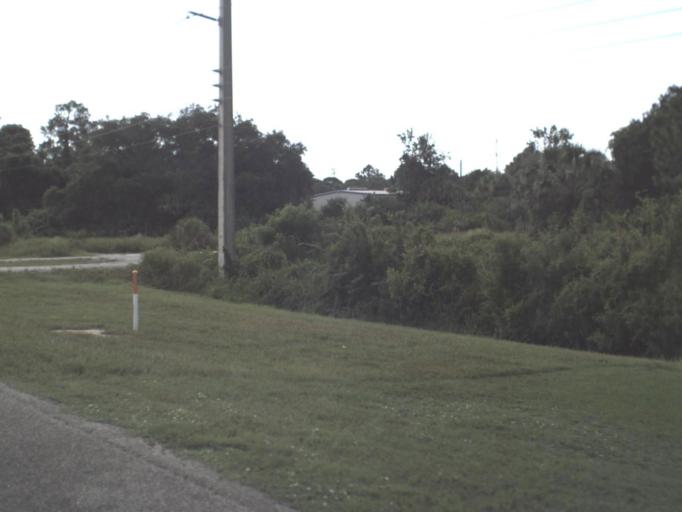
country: US
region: Florida
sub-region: Sarasota County
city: North Port
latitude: 27.0181
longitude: -82.1601
